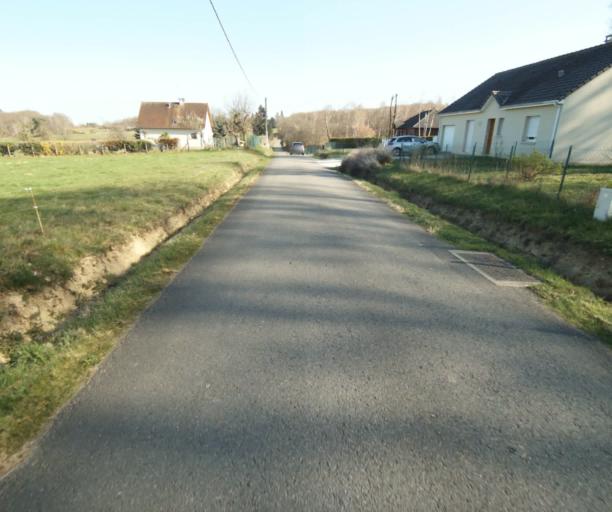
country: FR
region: Limousin
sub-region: Departement de la Correze
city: Saint-Clement
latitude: 45.3139
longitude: 1.6810
